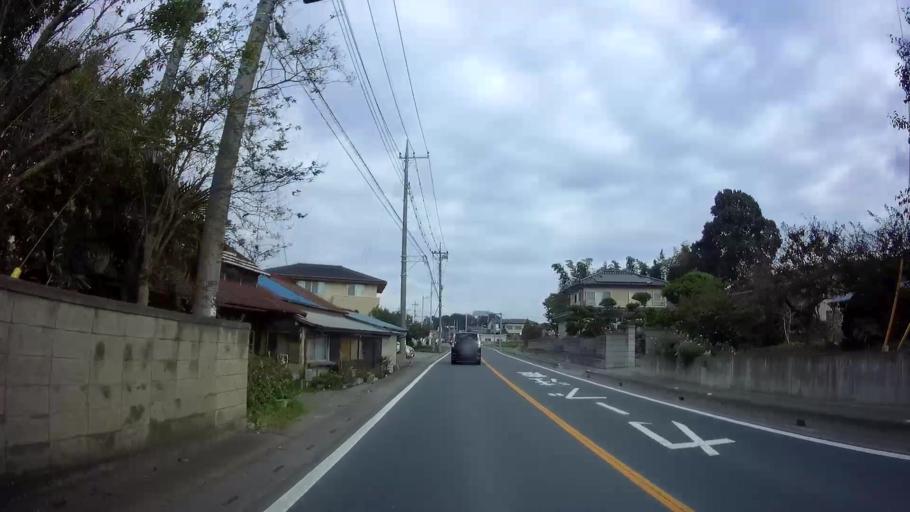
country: JP
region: Saitama
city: Okegawa
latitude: 36.0075
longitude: 139.5188
